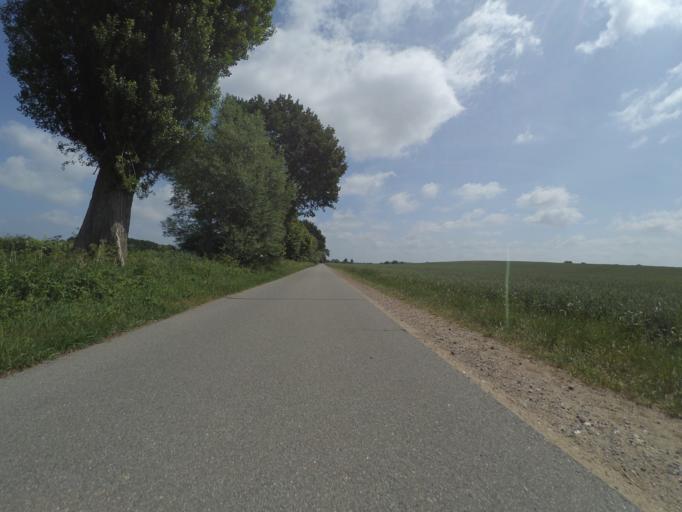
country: DE
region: Mecklenburg-Vorpommern
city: Siggelkow
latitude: 53.4070
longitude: 11.9983
